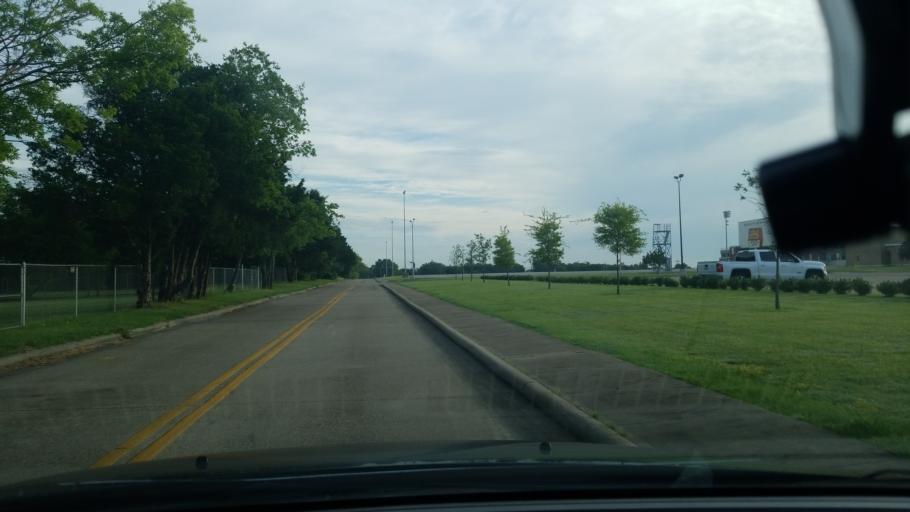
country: US
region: Texas
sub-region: Dallas County
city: Balch Springs
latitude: 32.7614
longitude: -96.6372
